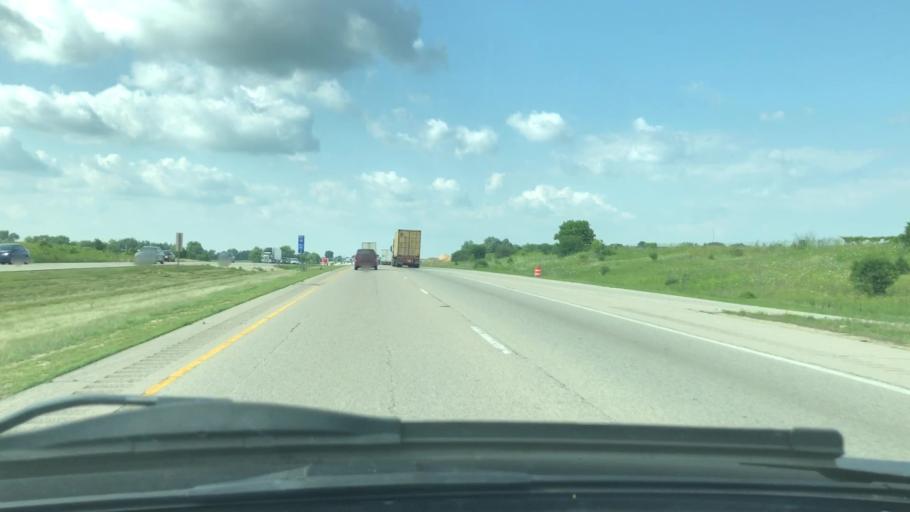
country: US
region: Wisconsin
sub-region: Rock County
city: Beloit
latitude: 42.5304
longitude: -88.9751
